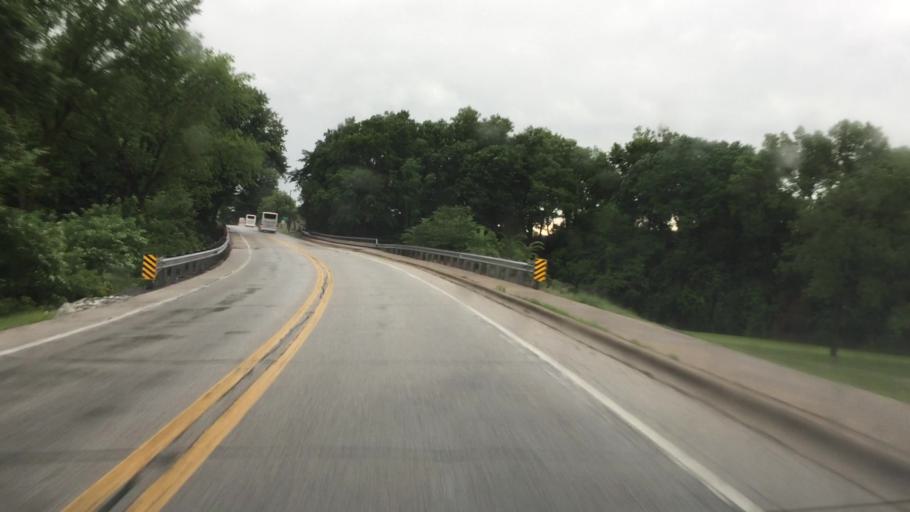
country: US
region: Illinois
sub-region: Hancock County
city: Hamilton
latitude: 40.4045
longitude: -91.3520
